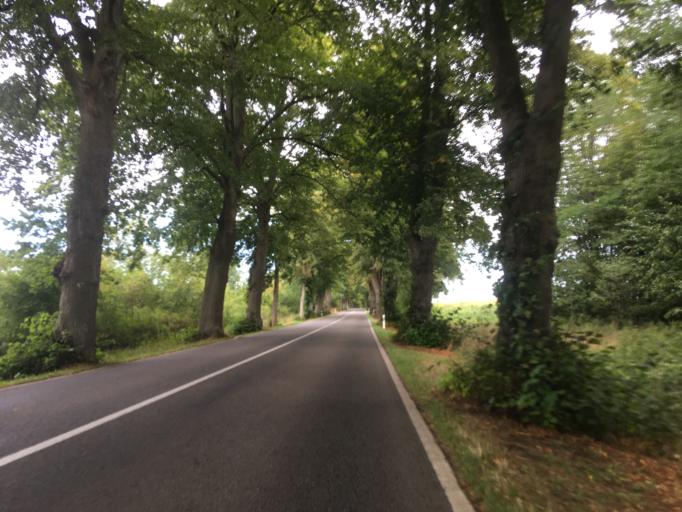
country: DE
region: Brandenburg
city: Templin
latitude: 53.1917
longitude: 13.5636
